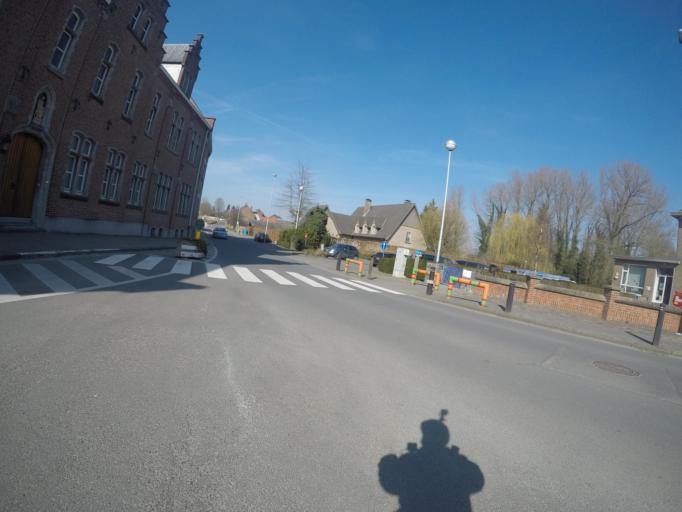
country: BE
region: Flanders
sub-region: Provincie Oost-Vlaanderen
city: Sint-Maria-Lierde
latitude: 50.7859
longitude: 3.8409
